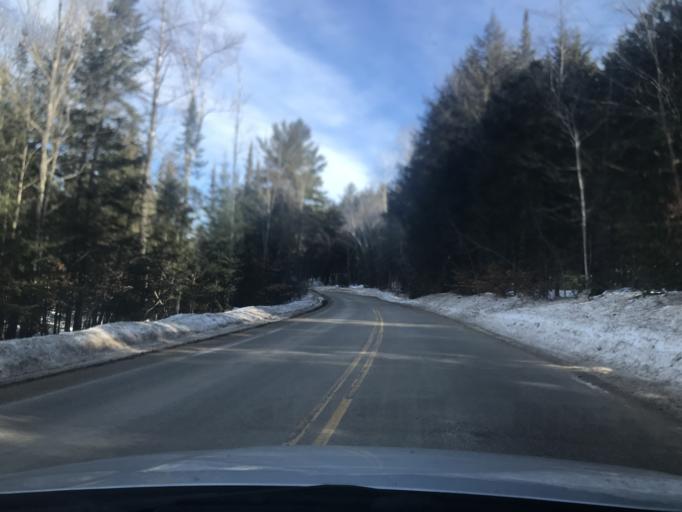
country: US
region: Michigan
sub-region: Dickinson County
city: Kingsford
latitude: 45.4080
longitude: -88.3670
